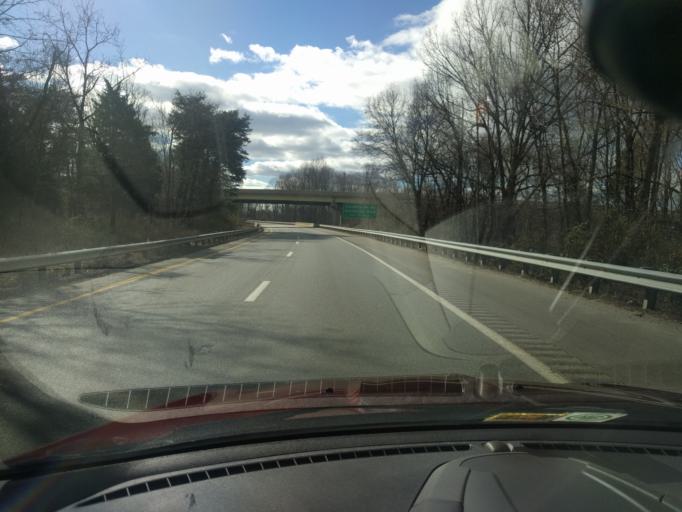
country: US
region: Virginia
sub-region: City of Lynchburg
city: West Lynchburg
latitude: 37.3627
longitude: -79.1647
